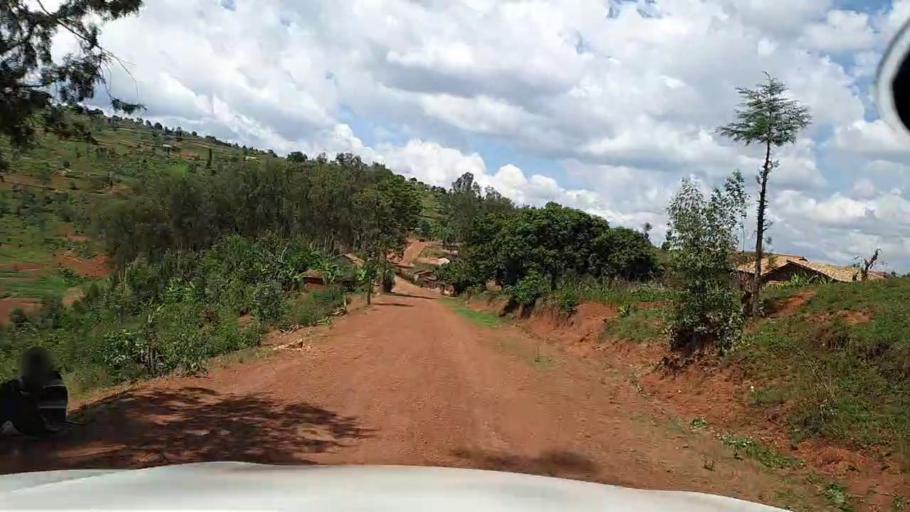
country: RW
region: Southern Province
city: Butare
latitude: -2.7512
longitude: 29.7020
